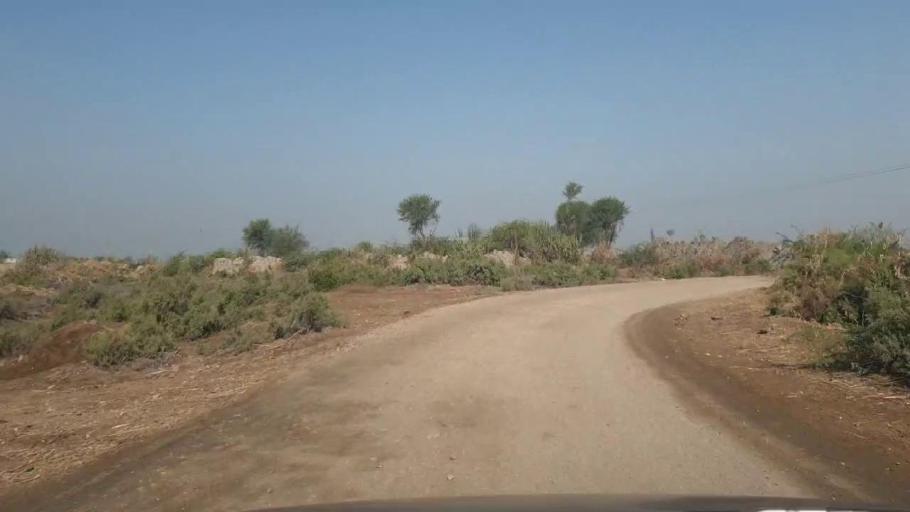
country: PK
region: Sindh
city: Mirwah Gorchani
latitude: 25.3736
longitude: 69.1866
